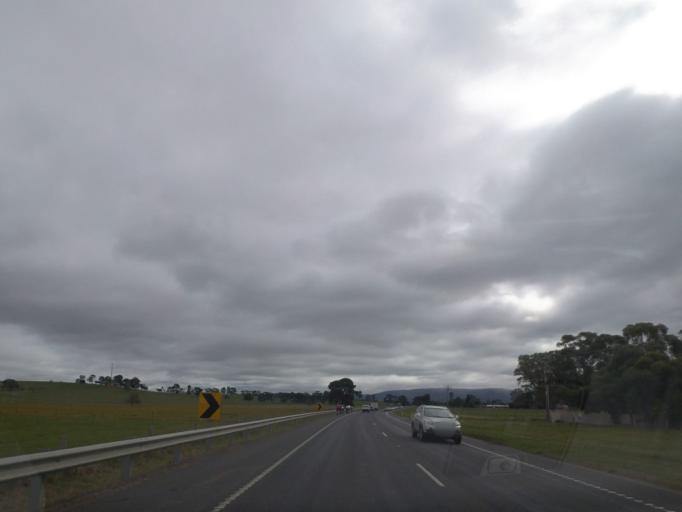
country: AU
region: Victoria
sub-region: Whittlesea
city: Whittlesea
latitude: -37.5487
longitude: 145.1090
